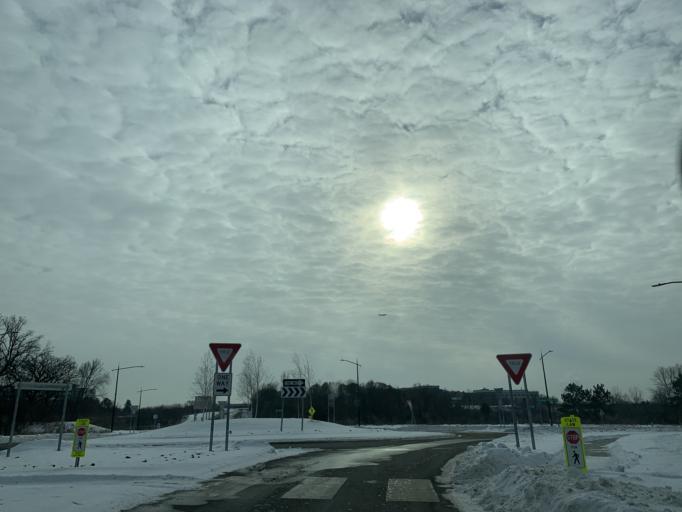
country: US
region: Minnesota
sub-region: Dakota County
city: Mendota Heights
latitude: 44.8571
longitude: -93.1112
